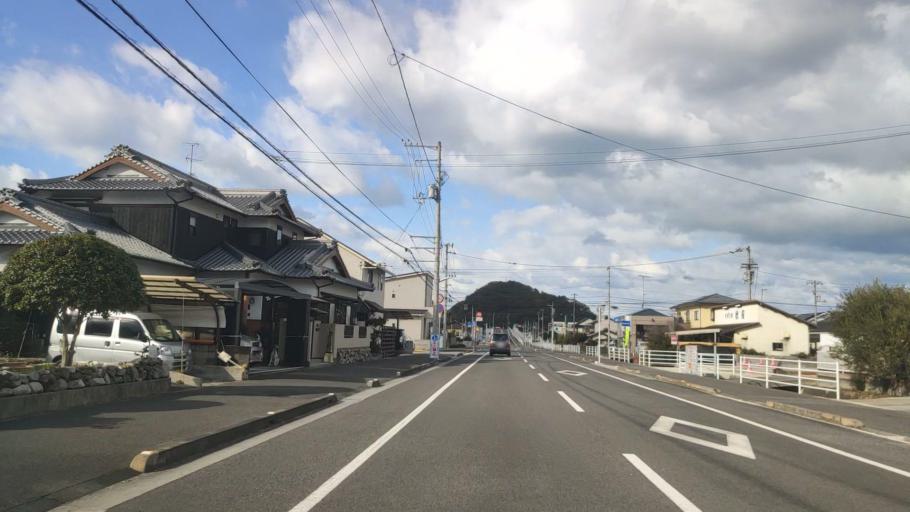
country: JP
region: Ehime
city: Hojo
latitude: 33.9706
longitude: 132.7788
